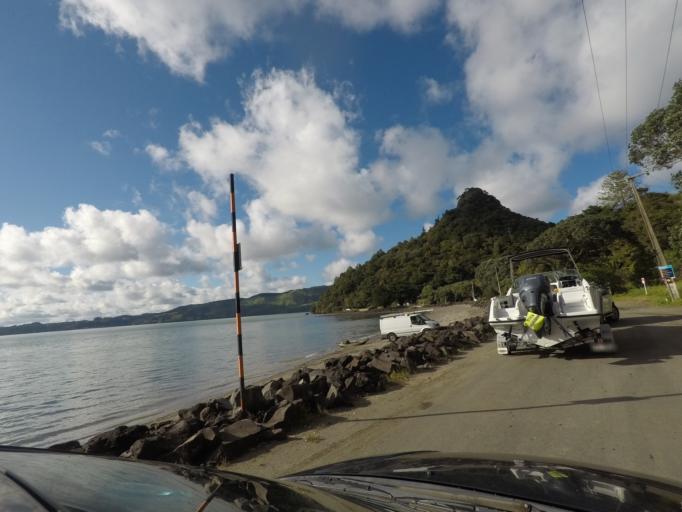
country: NZ
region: Auckland
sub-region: Auckland
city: Titirangi
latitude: -37.0146
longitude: 174.5588
